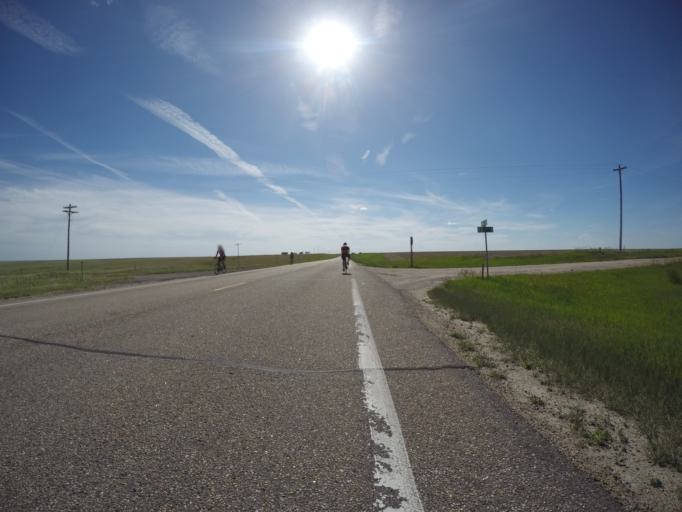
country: US
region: Kansas
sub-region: Cheyenne County
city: Saint Francis
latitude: 39.7567
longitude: -101.9747
